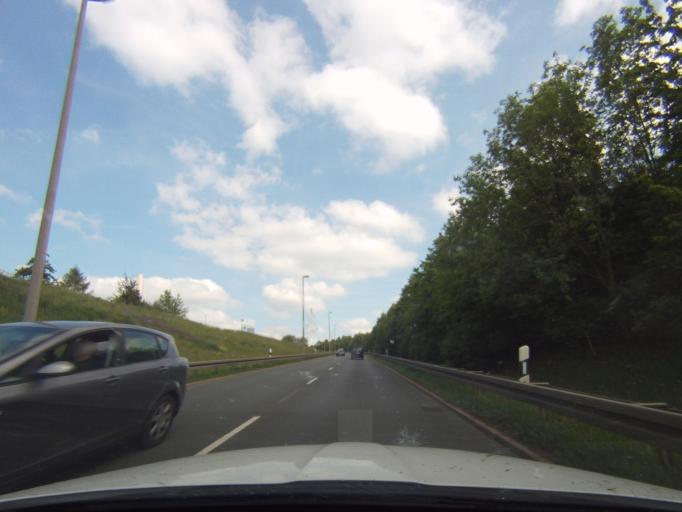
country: DE
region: Thuringia
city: Gera
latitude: 50.8609
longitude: 12.0980
